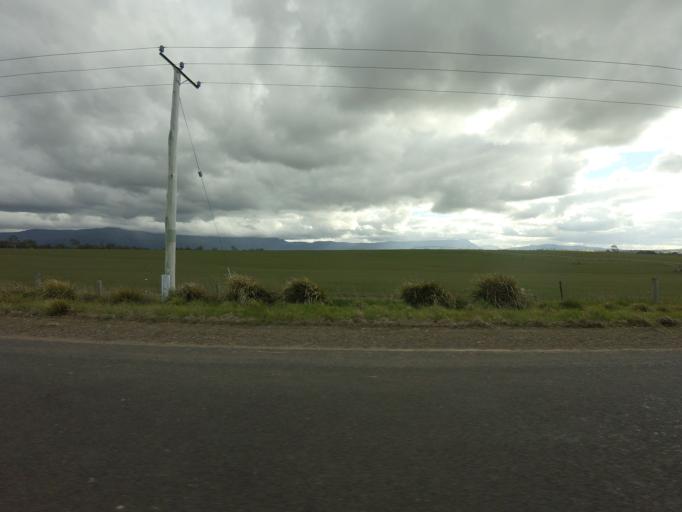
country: AU
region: Tasmania
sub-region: Northern Midlands
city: Longford
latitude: -41.7600
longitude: 147.0827
